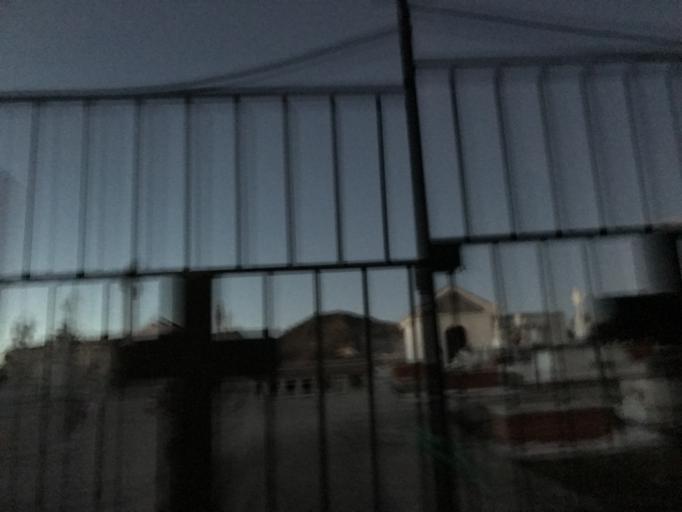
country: ES
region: Andalusia
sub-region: Provincia de Granada
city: Beas de Granada
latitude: 37.2188
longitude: -3.4771
